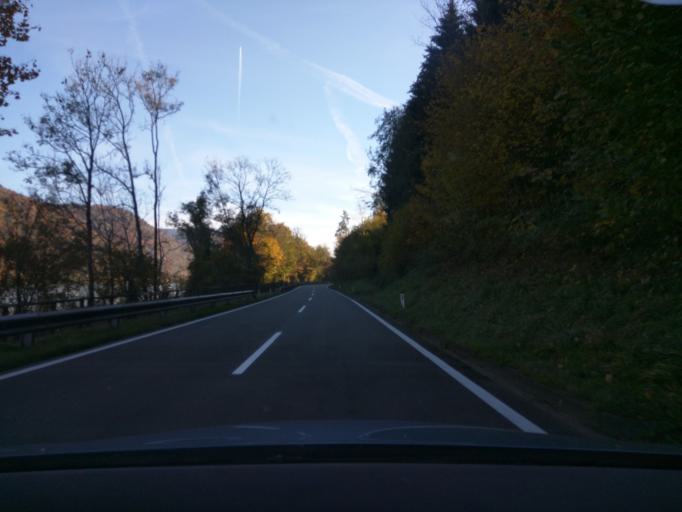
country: DE
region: Bavaria
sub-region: Lower Bavaria
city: Obernzell
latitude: 48.5332
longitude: 13.6647
